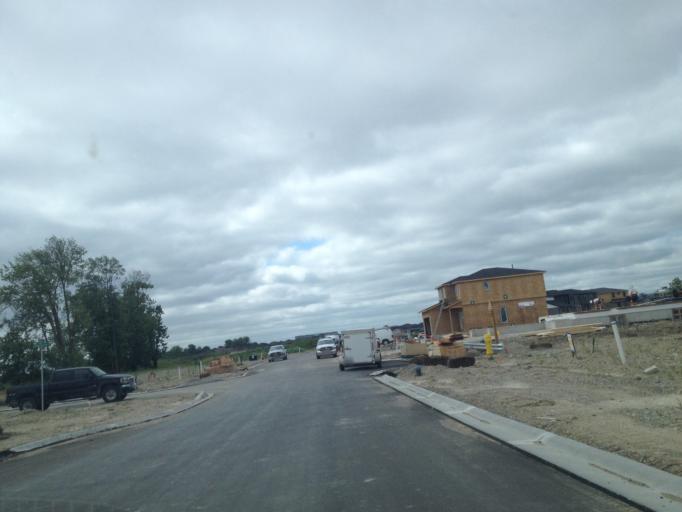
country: CA
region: Ontario
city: London
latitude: 43.0228
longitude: -81.3299
